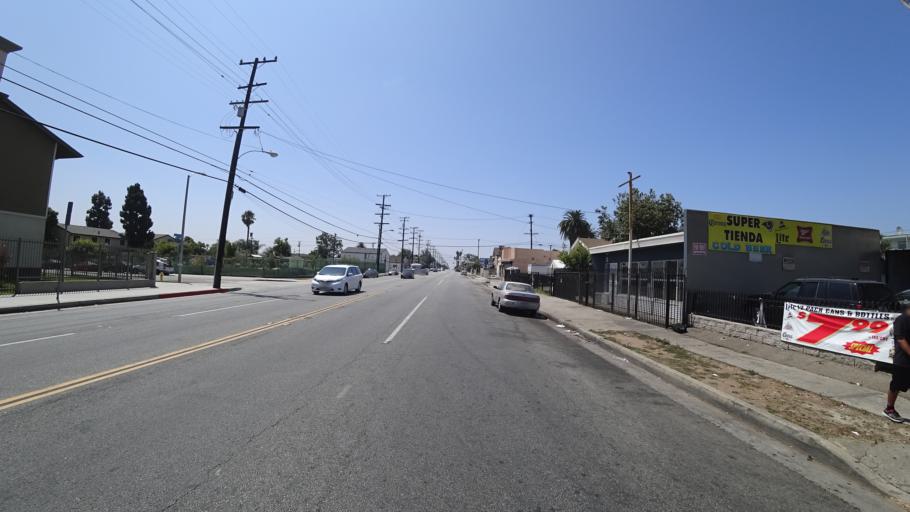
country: US
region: California
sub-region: Los Angeles County
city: Westmont
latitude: 33.9415
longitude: -118.3003
